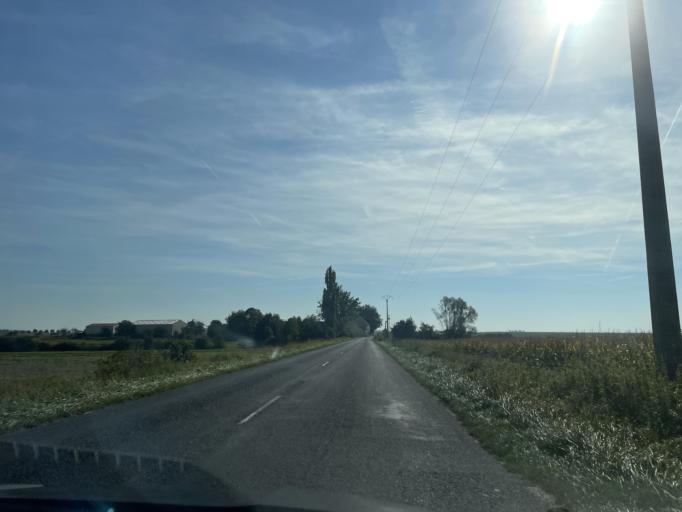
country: FR
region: Ile-de-France
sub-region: Departement de Seine-et-Marne
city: Coulommiers
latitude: 48.8789
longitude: 3.0765
